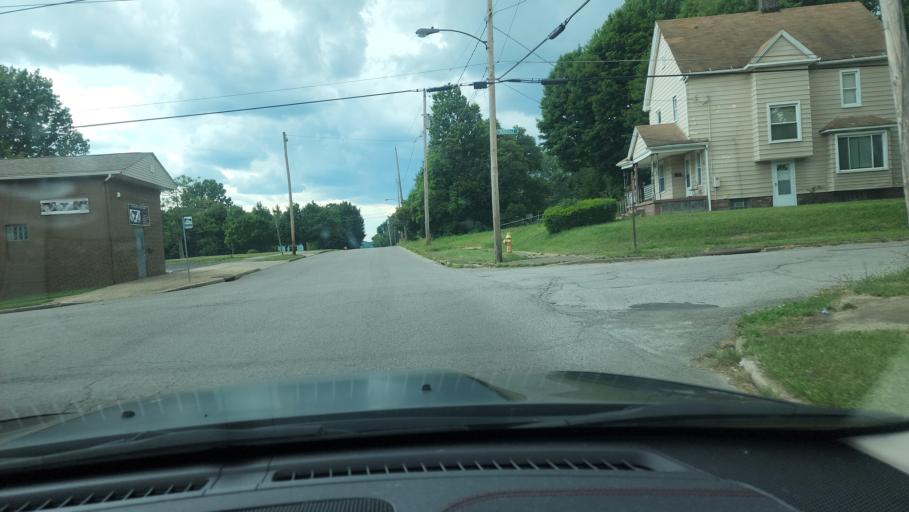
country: US
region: Ohio
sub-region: Mahoning County
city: Youngstown
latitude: 41.0950
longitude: -80.6257
